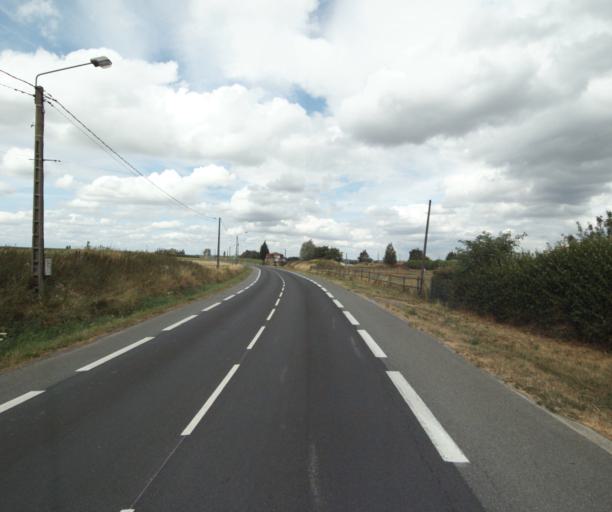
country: FR
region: Nord-Pas-de-Calais
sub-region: Departement du Nord
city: Linselles
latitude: 50.7546
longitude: 3.0790
